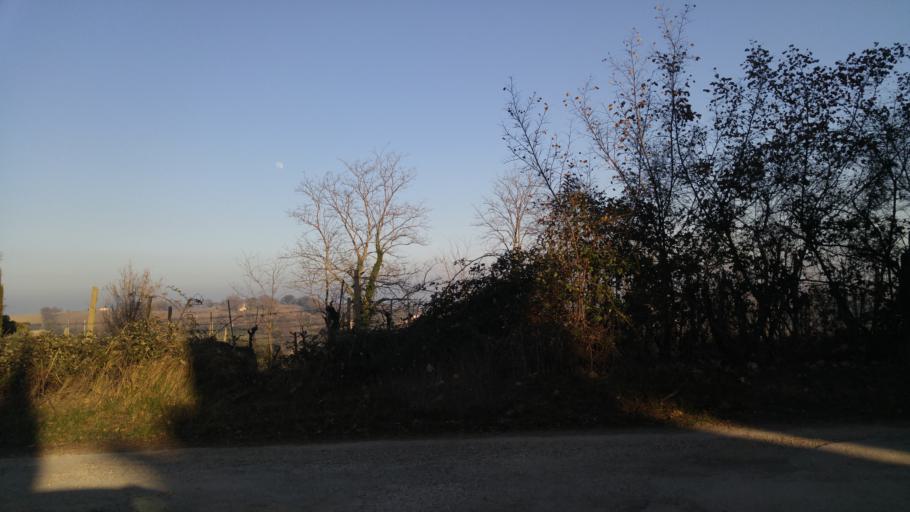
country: IT
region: The Marches
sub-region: Provincia di Pesaro e Urbino
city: Fenile
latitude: 43.8587
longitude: 12.9583
